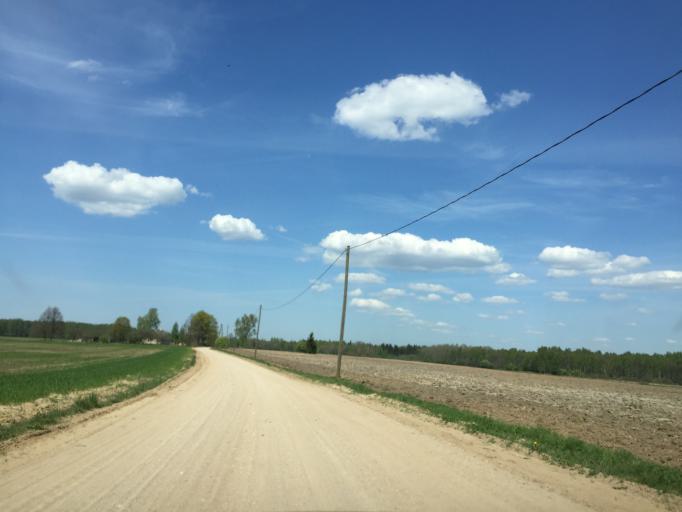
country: LV
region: Limbazu Rajons
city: Limbazi
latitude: 57.3515
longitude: 24.6497
